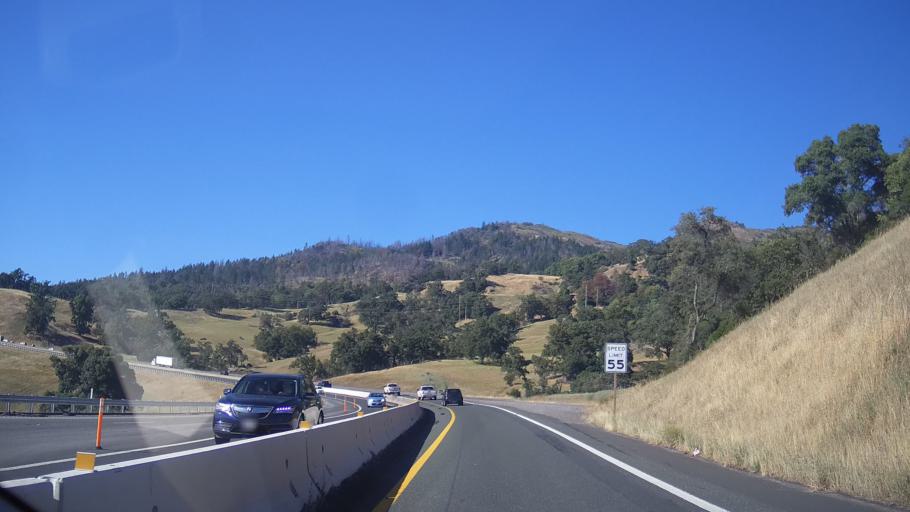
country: US
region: California
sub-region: Mendocino County
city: Redwood Valley
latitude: 39.3101
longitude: -123.2987
